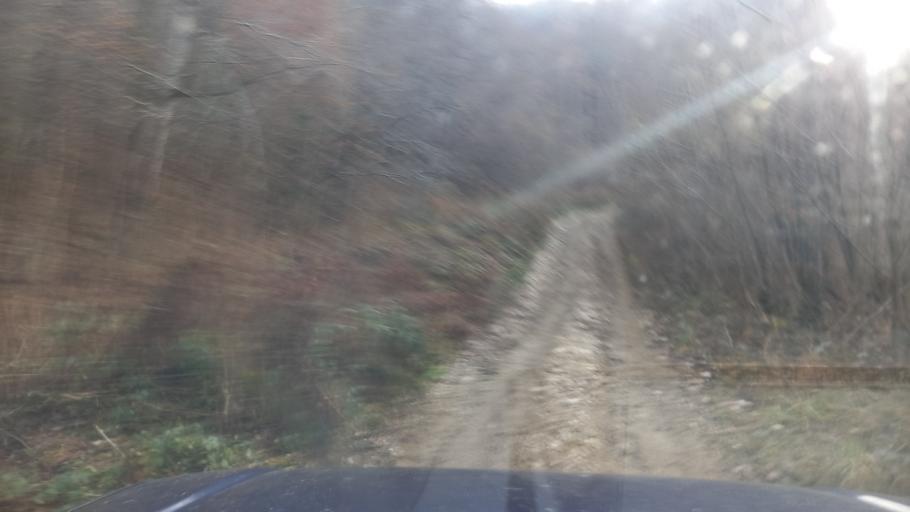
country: RU
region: Krasnodarskiy
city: Neftegorsk
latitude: 44.2076
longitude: 39.7094
